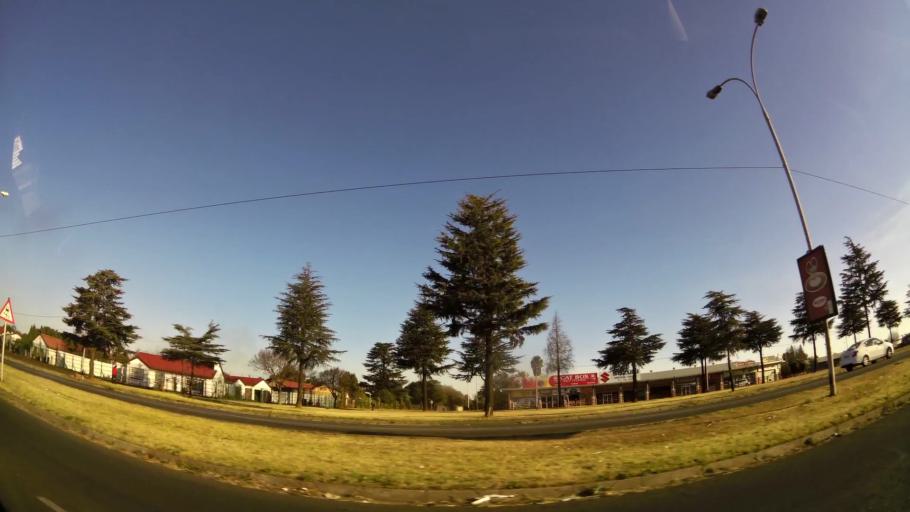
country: ZA
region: Gauteng
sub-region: City of Johannesburg Metropolitan Municipality
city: Roodepoort
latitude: -26.1459
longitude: 27.8828
